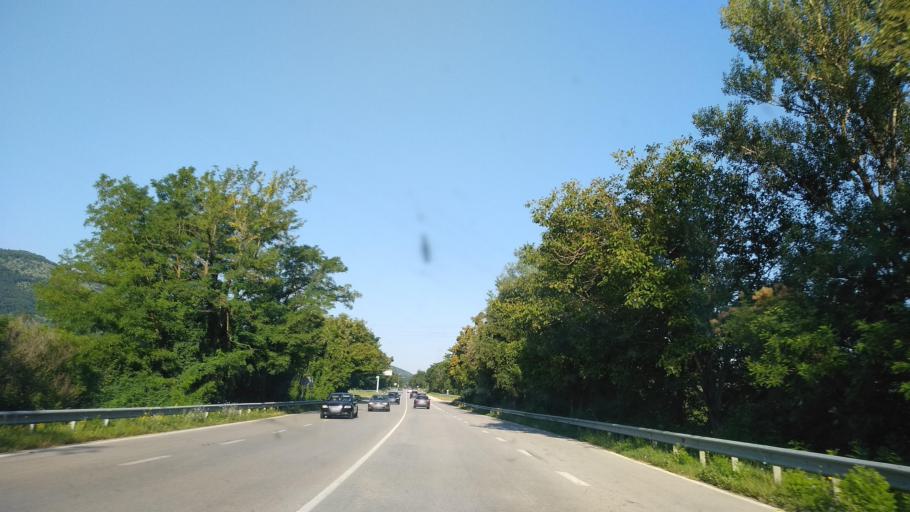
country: BG
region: Lovech
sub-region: Obshtina Lovech
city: Lovech
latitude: 43.0411
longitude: 24.7218
